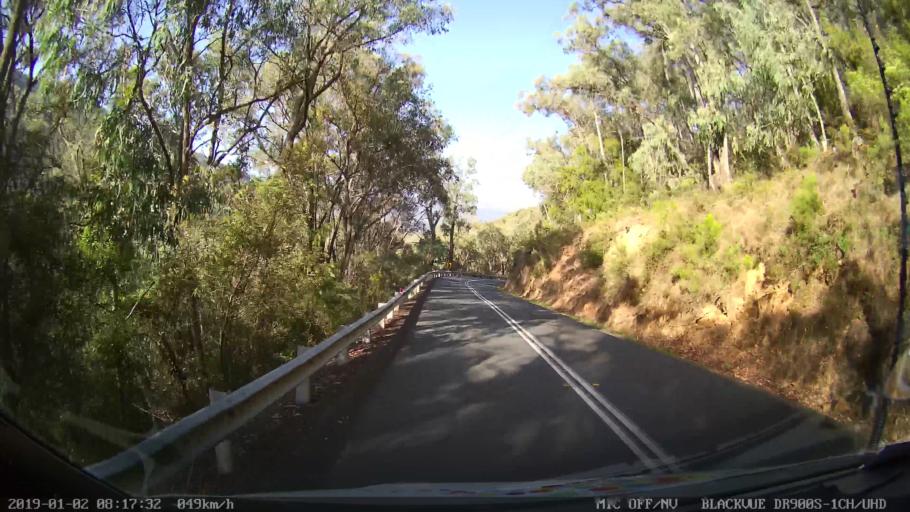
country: AU
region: New South Wales
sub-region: Tumut Shire
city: Tumut
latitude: -35.5804
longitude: 148.3233
